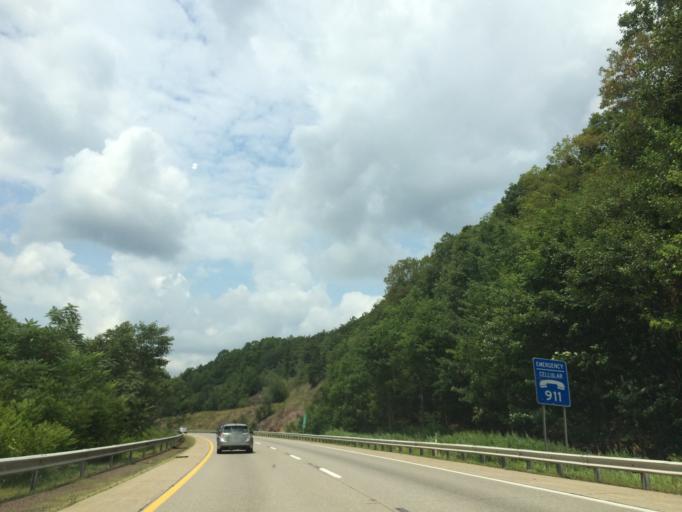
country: US
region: Pennsylvania
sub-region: Luzerne County
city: Nescopeck
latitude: 41.0191
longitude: -76.1731
